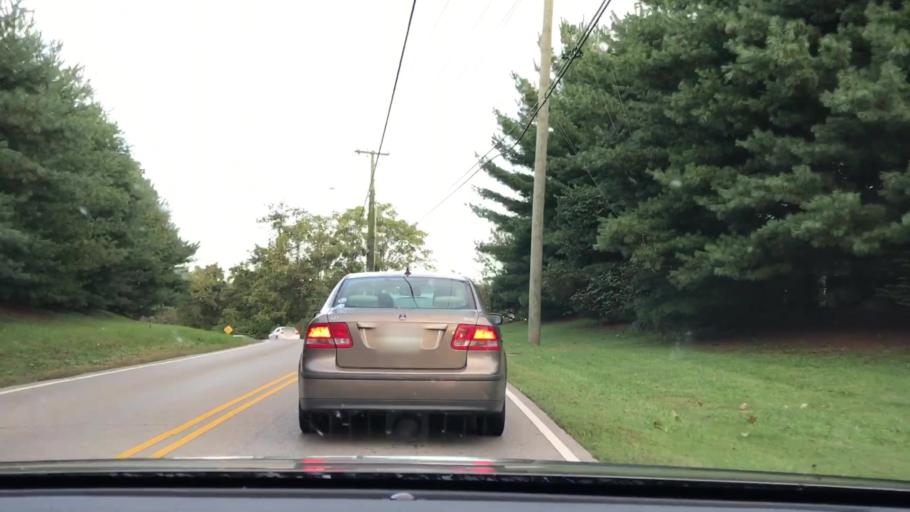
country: US
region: Tennessee
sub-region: Williamson County
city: Brentwood Estates
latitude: 36.0321
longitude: -86.7567
